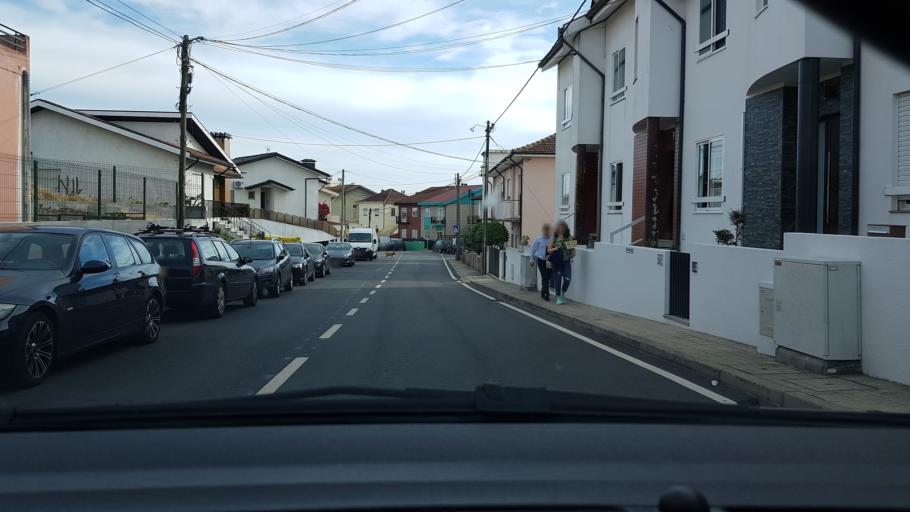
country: PT
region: Porto
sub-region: Gondomar
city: Rio Tinto
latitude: 41.1906
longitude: -8.5534
